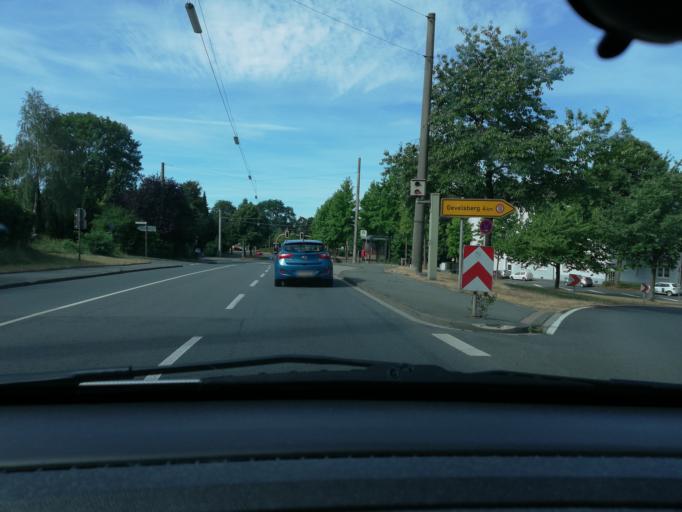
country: DE
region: North Rhine-Westphalia
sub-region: Regierungsbezirk Arnsberg
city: Schwelm
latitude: 51.2953
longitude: 7.3071
